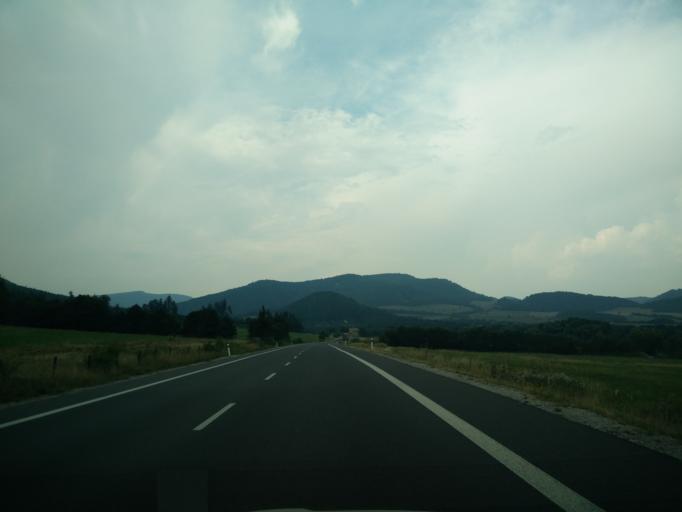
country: SK
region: Nitriansky
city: Handlova
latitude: 48.6392
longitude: 18.7729
